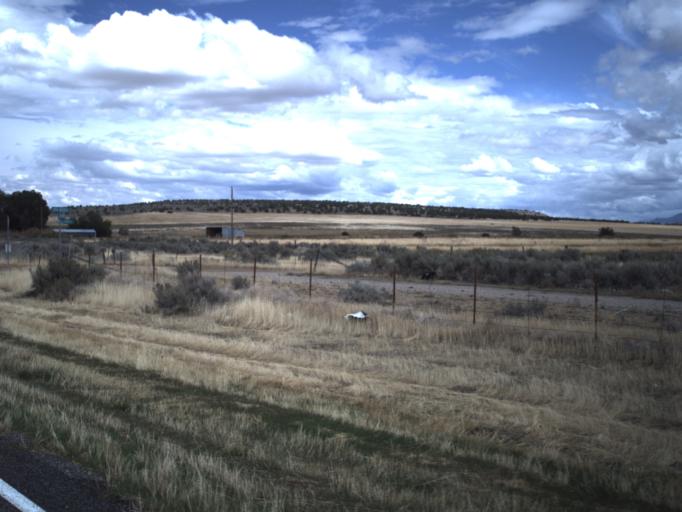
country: US
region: Utah
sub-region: Millard County
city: Fillmore
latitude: 38.9861
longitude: -112.4104
